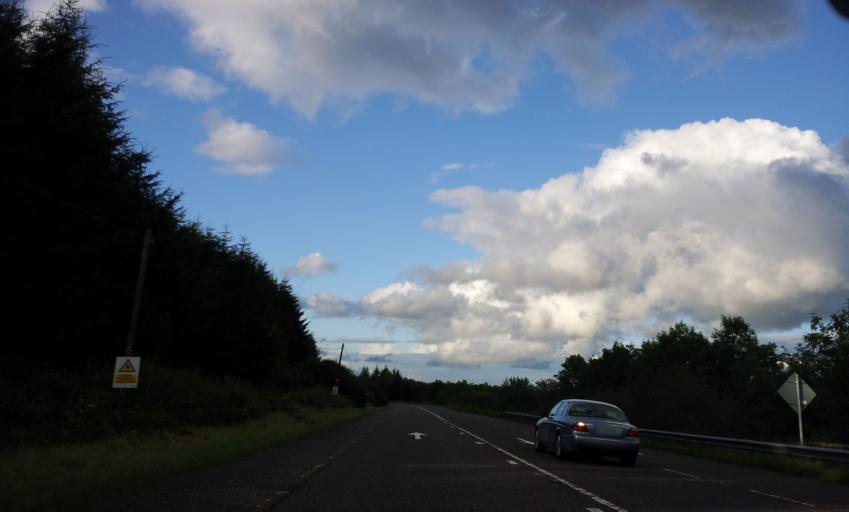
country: IE
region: Munster
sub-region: Ciarrai
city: Castleisland
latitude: 52.2785
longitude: -9.4105
